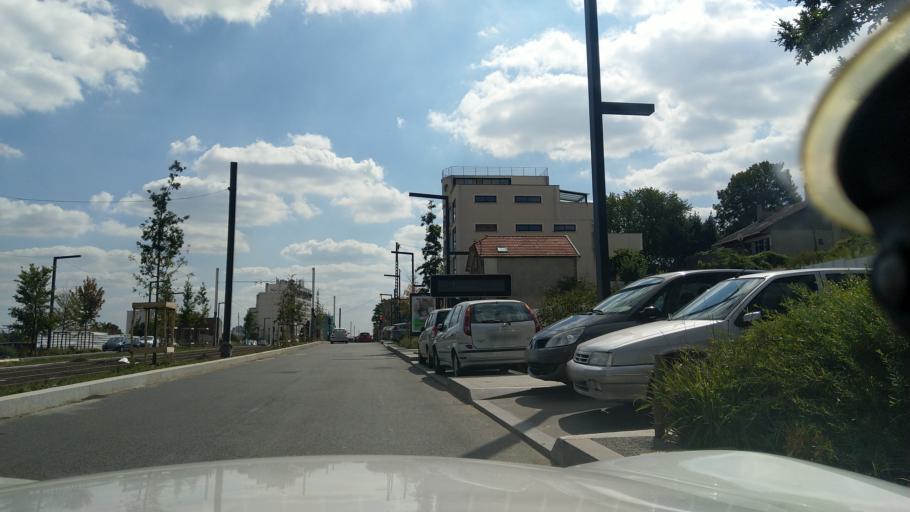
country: FR
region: Ile-de-France
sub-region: Departement du Val-de-Marne
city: Vitry-sur-Seine
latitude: 48.7772
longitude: 2.3971
